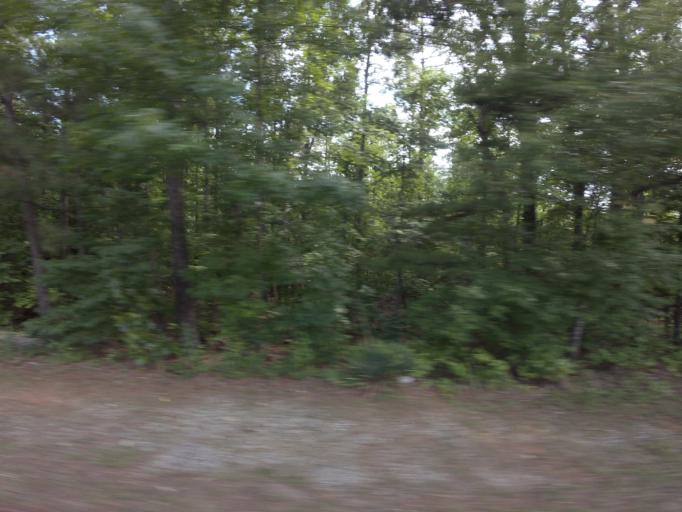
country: US
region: Georgia
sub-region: Fulton County
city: Johns Creek
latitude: 34.0310
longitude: -84.2319
